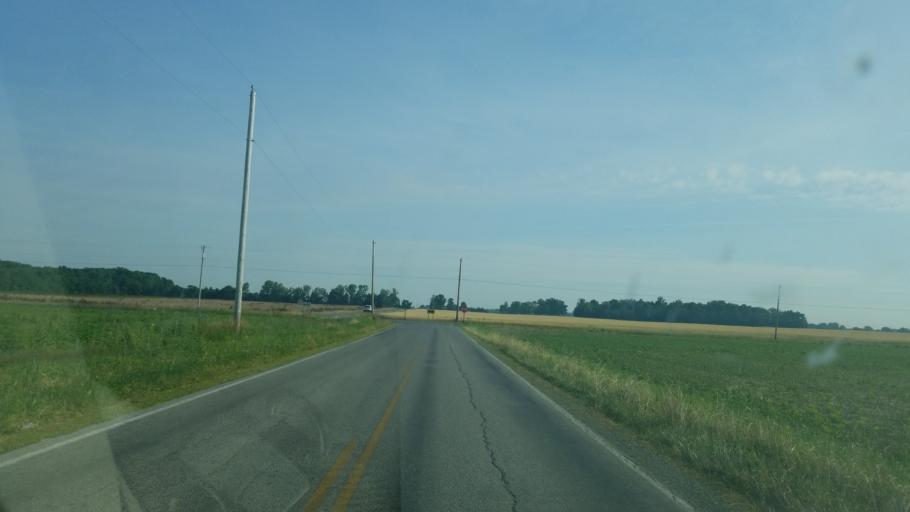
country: US
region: Ohio
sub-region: Hancock County
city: Arlington
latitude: 40.9060
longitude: -83.6985
